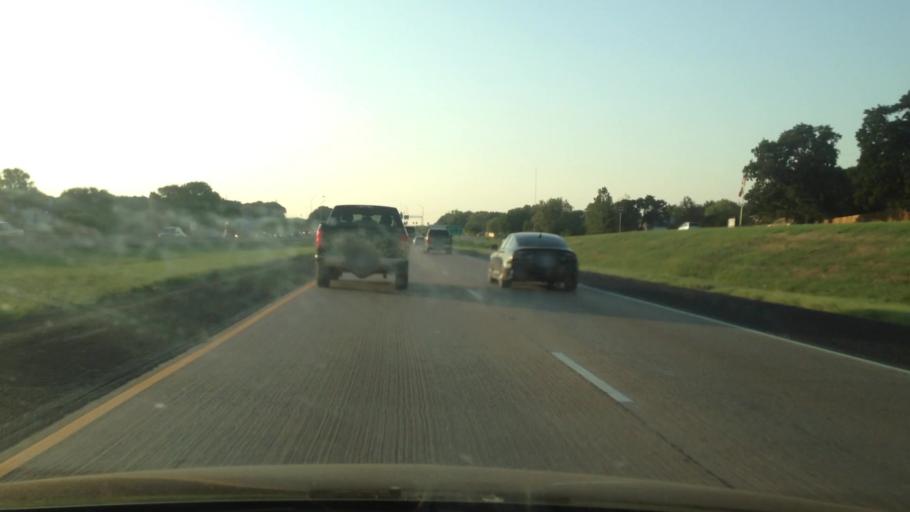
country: US
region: Texas
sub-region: Tarrant County
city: Kennedale
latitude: 32.6598
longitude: -97.1963
